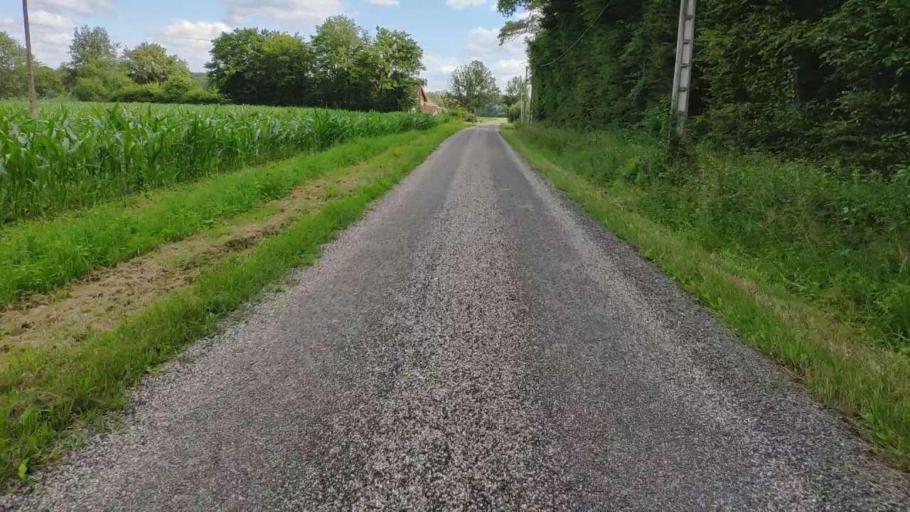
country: FR
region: Franche-Comte
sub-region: Departement du Jura
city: Bletterans
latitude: 46.8143
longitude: 5.4274
